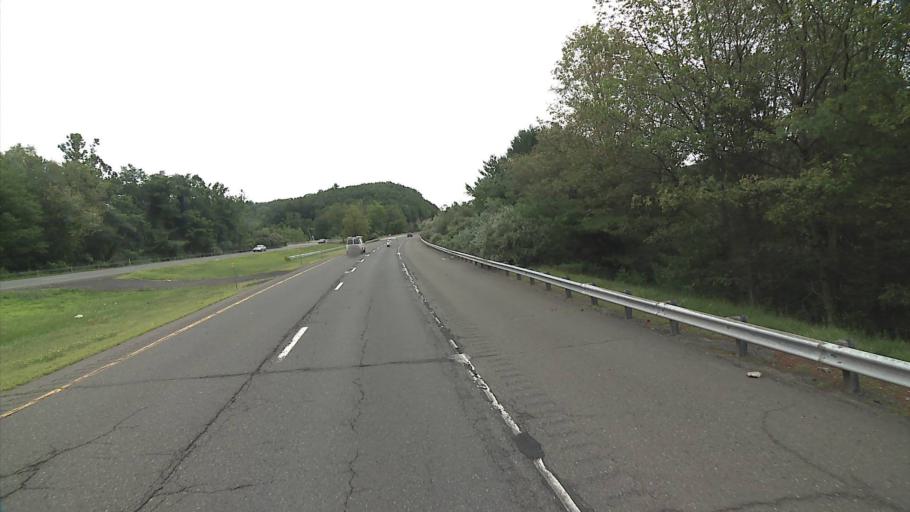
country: US
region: Connecticut
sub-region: Litchfield County
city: Thomaston
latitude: 41.6461
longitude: -73.0821
